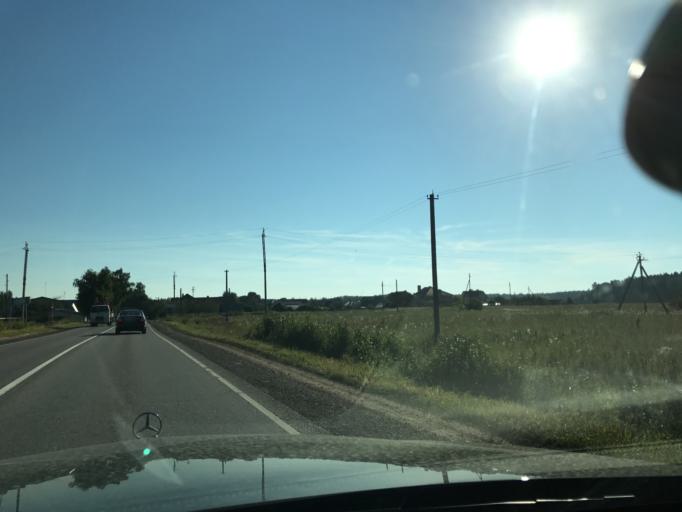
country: RU
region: Moskovskaya
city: Bakhchivandzhi
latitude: 55.8535
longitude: 38.1236
